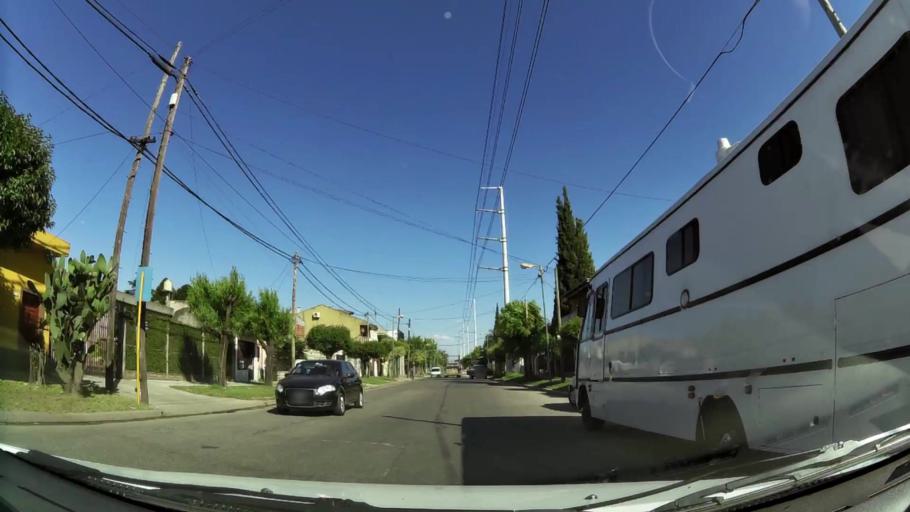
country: AR
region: Buenos Aires
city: Caseros
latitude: -34.5566
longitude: -58.5900
